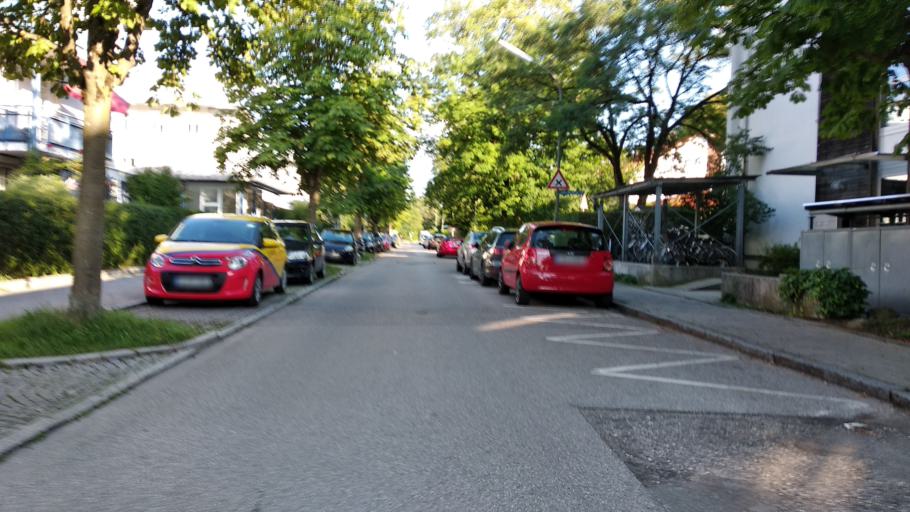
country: DE
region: Bavaria
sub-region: Upper Bavaria
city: Haar
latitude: 48.1121
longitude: 11.7210
